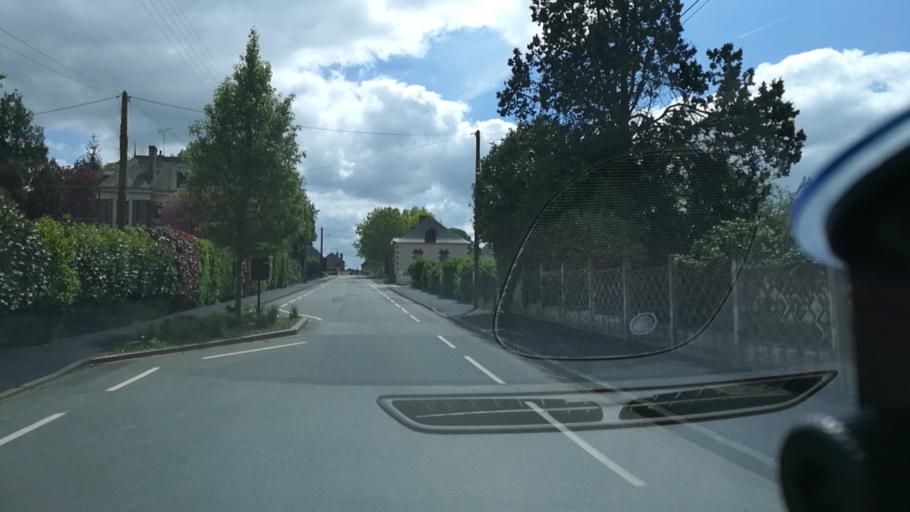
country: FR
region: Brittany
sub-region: Departement d'Ille-et-Vilaine
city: Retiers
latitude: 47.9103
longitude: -1.3794
